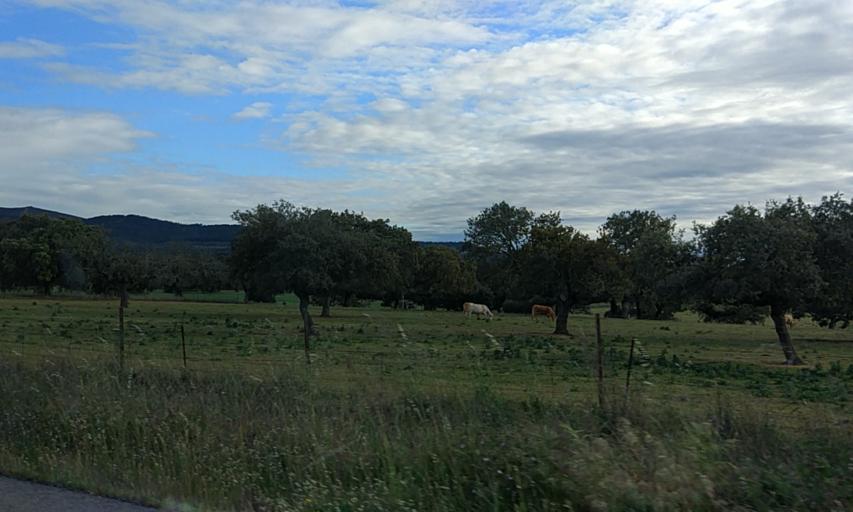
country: ES
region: Extremadura
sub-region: Provincia de Caceres
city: Pedroso de Acim
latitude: 39.8642
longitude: -6.4331
